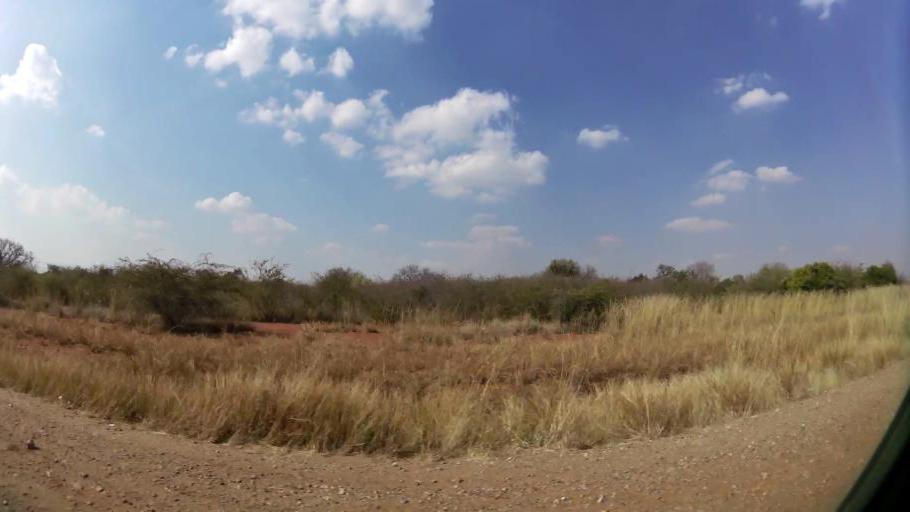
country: ZA
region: North-West
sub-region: Bojanala Platinum District Municipality
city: Mogwase
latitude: -25.4659
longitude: 27.0873
